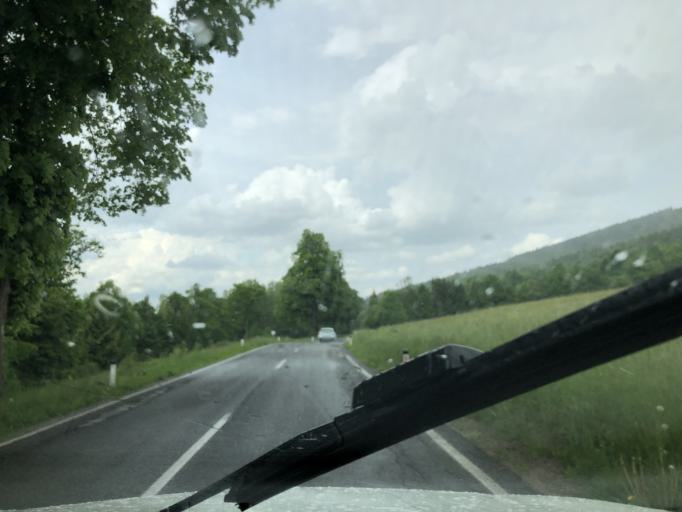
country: SI
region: Cerknica
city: Cerknica
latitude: 45.7832
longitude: 14.3850
